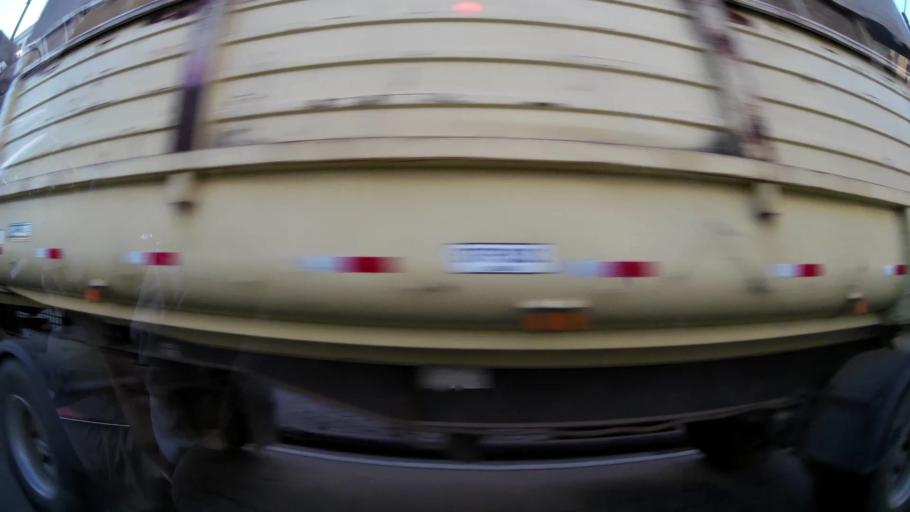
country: UY
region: Montevideo
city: Montevideo
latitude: -34.8866
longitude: -56.1981
